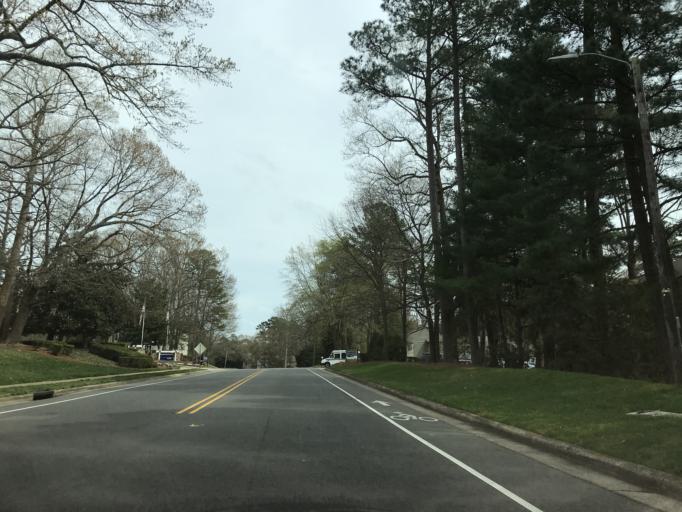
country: US
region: North Carolina
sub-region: Wake County
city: West Raleigh
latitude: 35.8862
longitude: -78.6773
